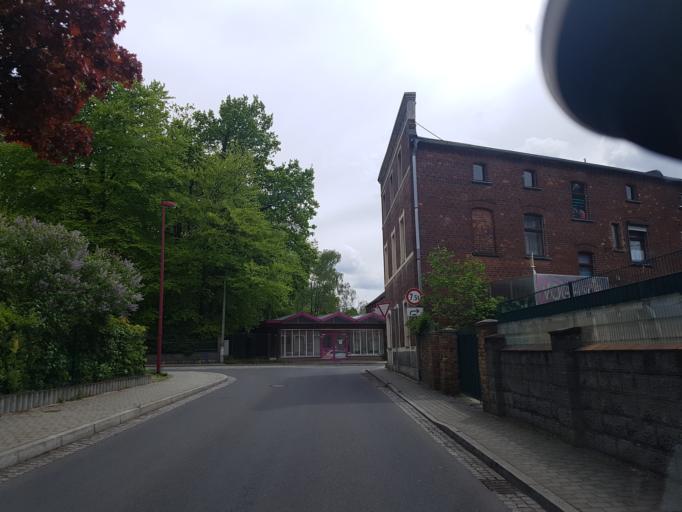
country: DE
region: Brandenburg
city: Tschernitz
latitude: 51.6140
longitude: 14.5922
